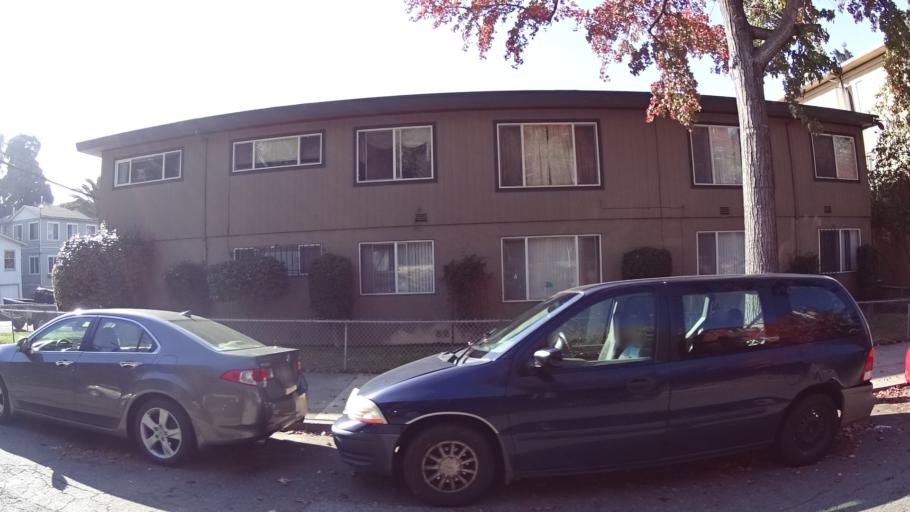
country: US
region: California
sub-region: Alameda County
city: Piedmont
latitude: 37.8207
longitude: -122.2533
